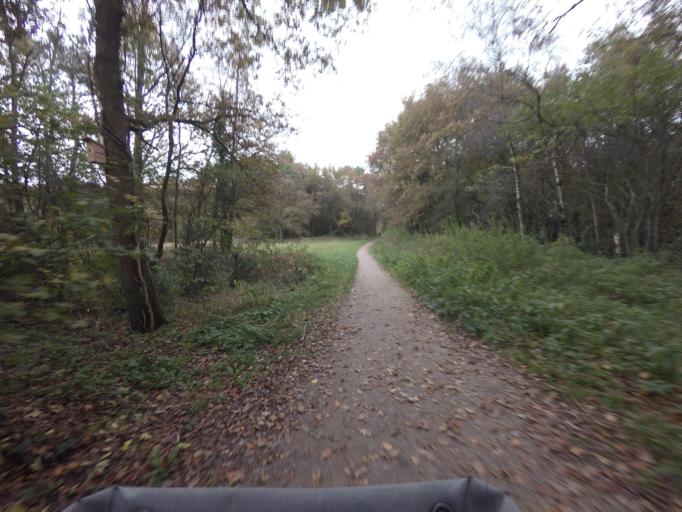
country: NL
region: North Holland
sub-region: Gemeente Laren
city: Laren
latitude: 52.2454
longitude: 5.2284
